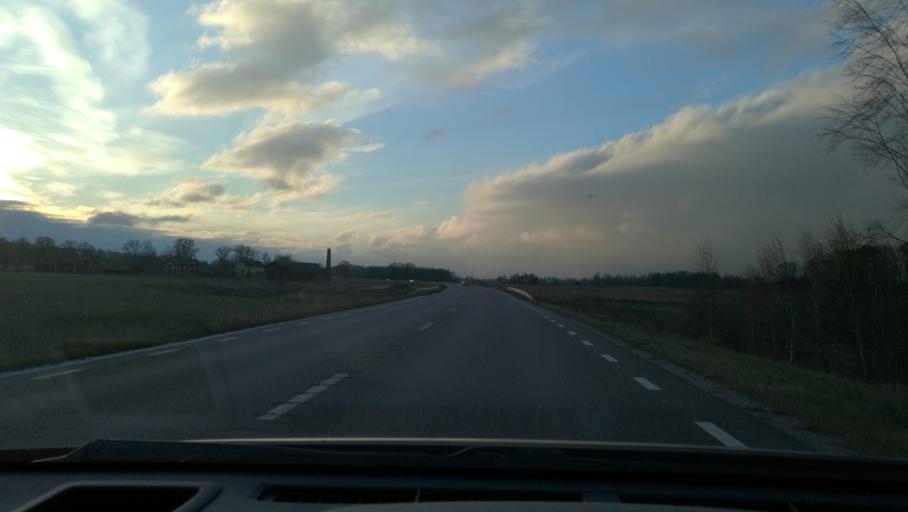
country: SE
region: Soedermanland
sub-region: Katrineholms Kommun
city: Katrineholm
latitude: 59.1555
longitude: 16.0941
